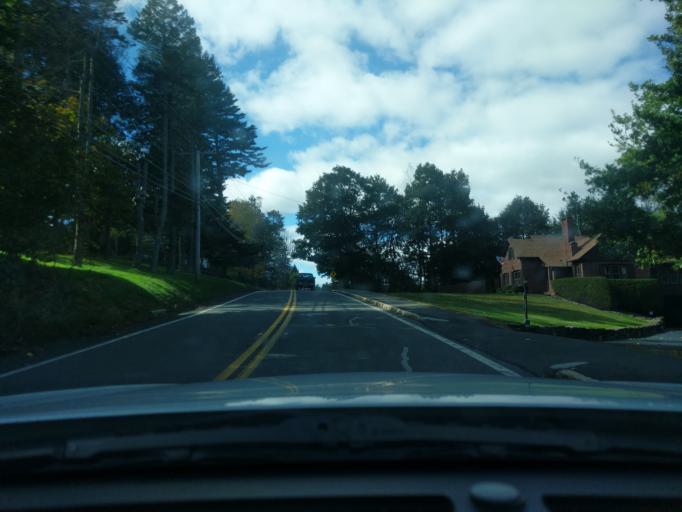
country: US
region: Massachusetts
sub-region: Hampden County
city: Granville
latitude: 42.1785
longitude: -72.9209
